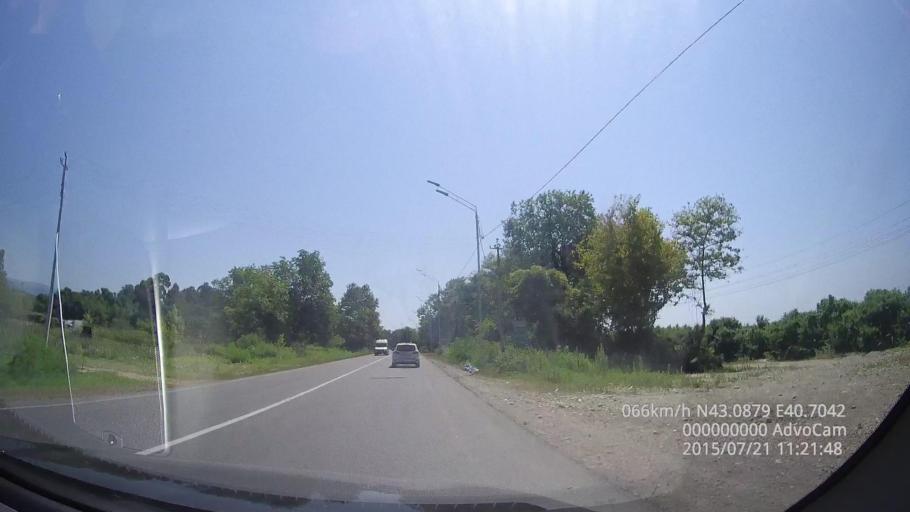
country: GE
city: P'rimorsk'oe
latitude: 43.0875
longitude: 40.7039
